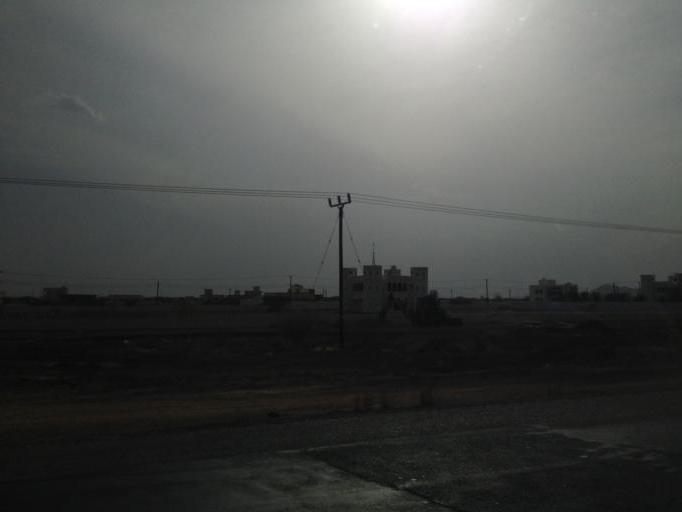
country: OM
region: Ash Sharqiyah
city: Al Qabil
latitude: 22.6155
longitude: 58.6612
